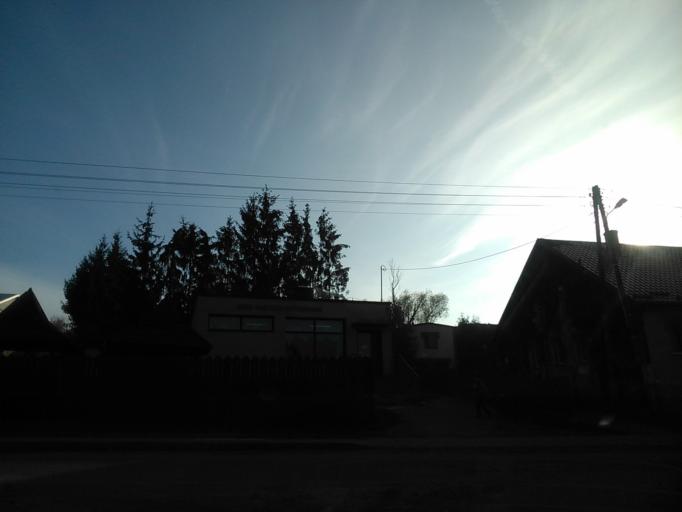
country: PL
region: Warmian-Masurian Voivodeship
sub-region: Powiat dzialdowski
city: Rybno
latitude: 53.2758
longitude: 19.9578
